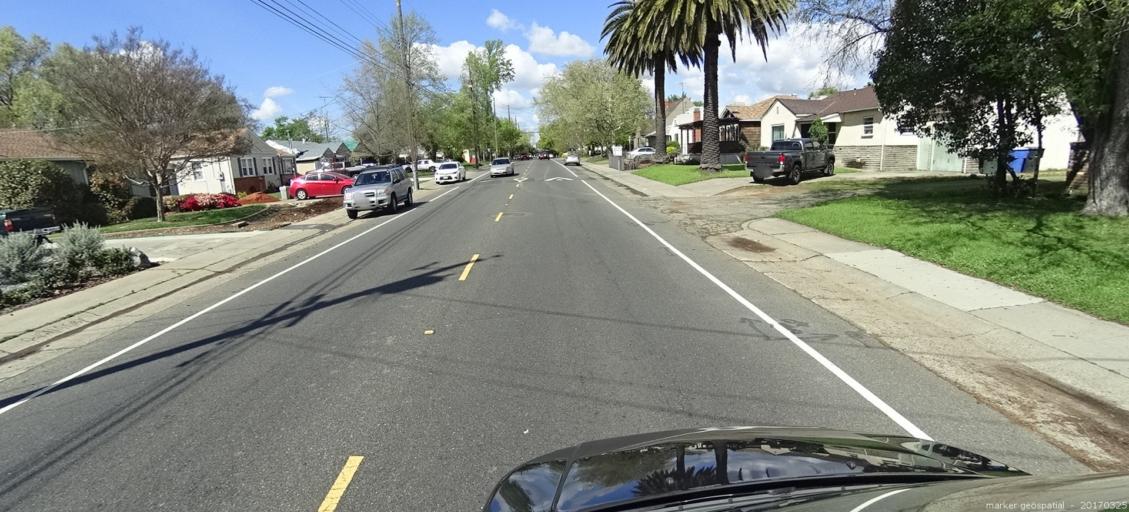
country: US
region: California
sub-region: Sacramento County
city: Parkway
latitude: 38.5490
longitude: -121.4366
